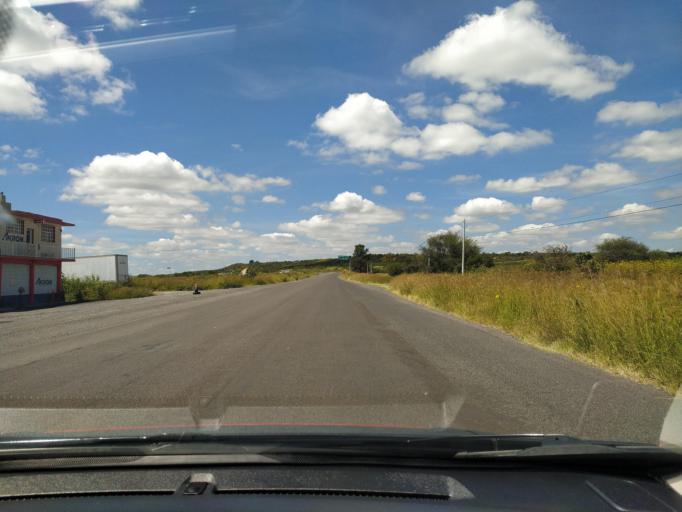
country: MX
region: Jalisco
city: San Diego de Alejandria
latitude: 20.9991
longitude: -102.0024
